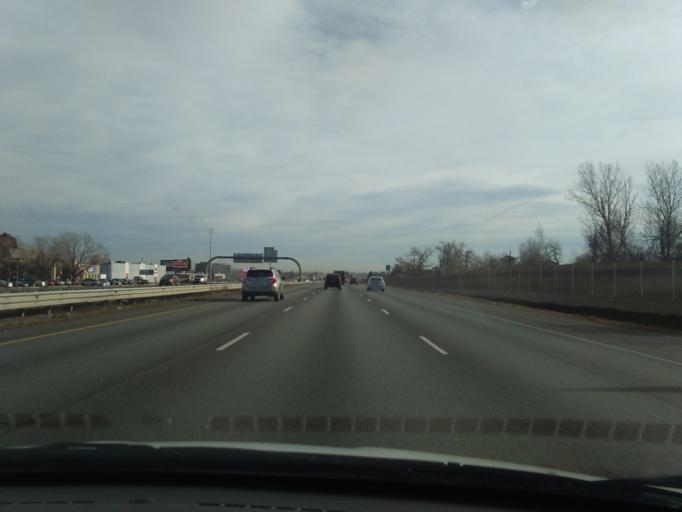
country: US
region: Colorado
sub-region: Jefferson County
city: Arvada
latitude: 39.7841
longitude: -105.1200
